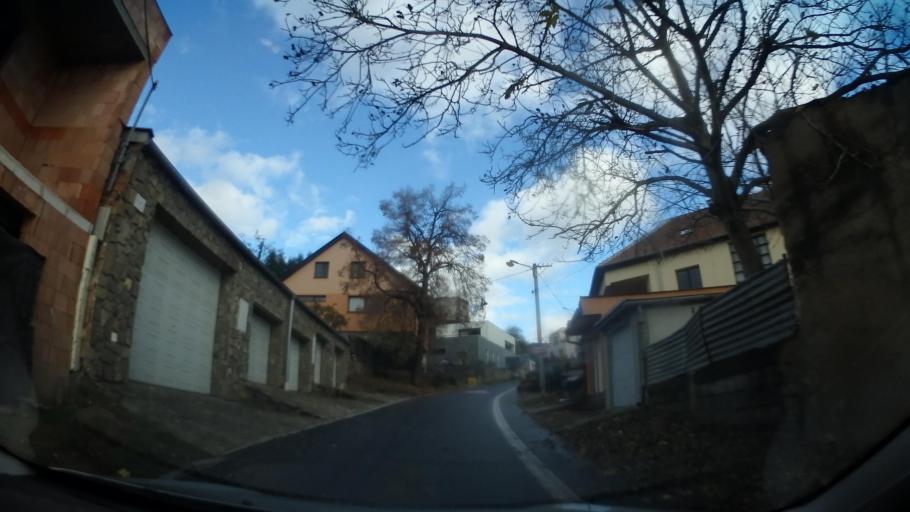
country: CZ
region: South Moravian
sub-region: Okres Brno-Venkov
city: Rosice
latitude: 49.1797
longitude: 16.3914
